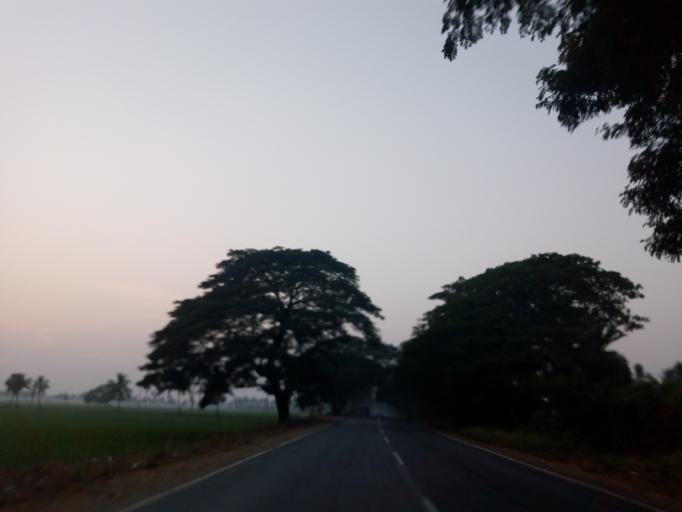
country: IN
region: Andhra Pradesh
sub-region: West Godavari
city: Tadepallegudem
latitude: 16.8202
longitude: 81.4827
